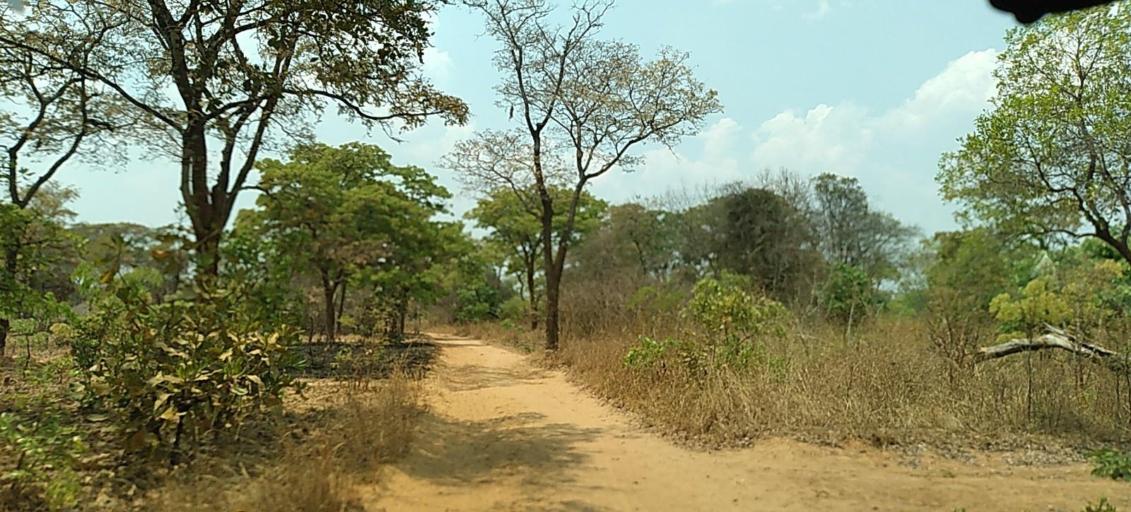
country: ZM
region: North-Western
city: Kabompo
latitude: -13.6454
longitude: 24.3778
